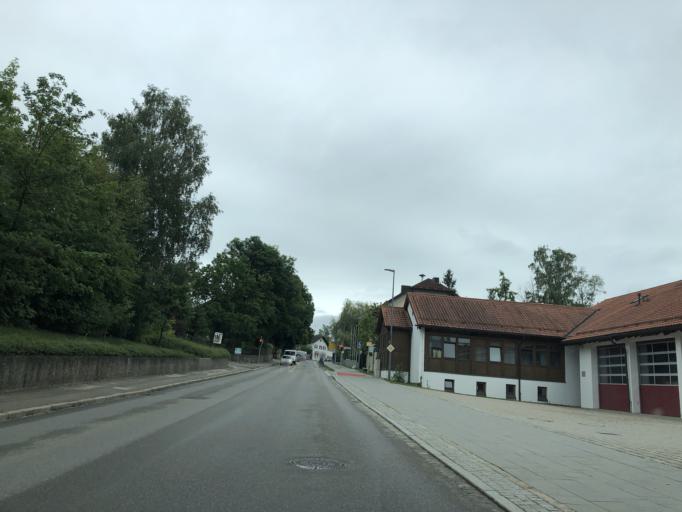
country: DE
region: Bavaria
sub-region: Upper Bavaria
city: Otterfing
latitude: 47.9115
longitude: 11.6741
